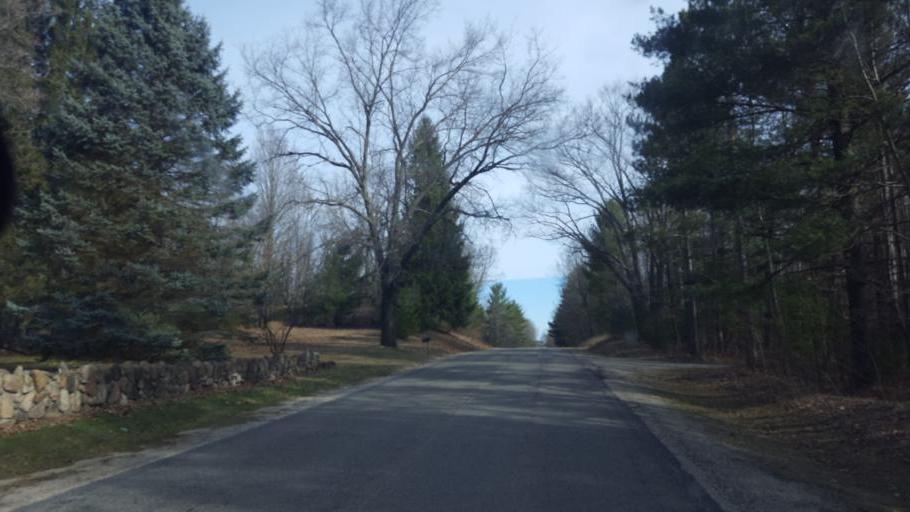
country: US
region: Michigan
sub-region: Montcalm County
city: Howard City
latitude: 43.5432
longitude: -85.5423
